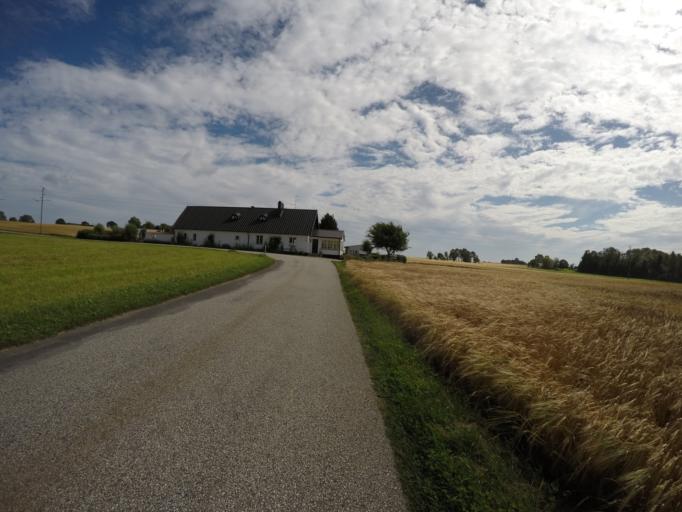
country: SE
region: Skane
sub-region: Simrishamns Kommun
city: Simrishamn
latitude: 55.4911
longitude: 14.2586
